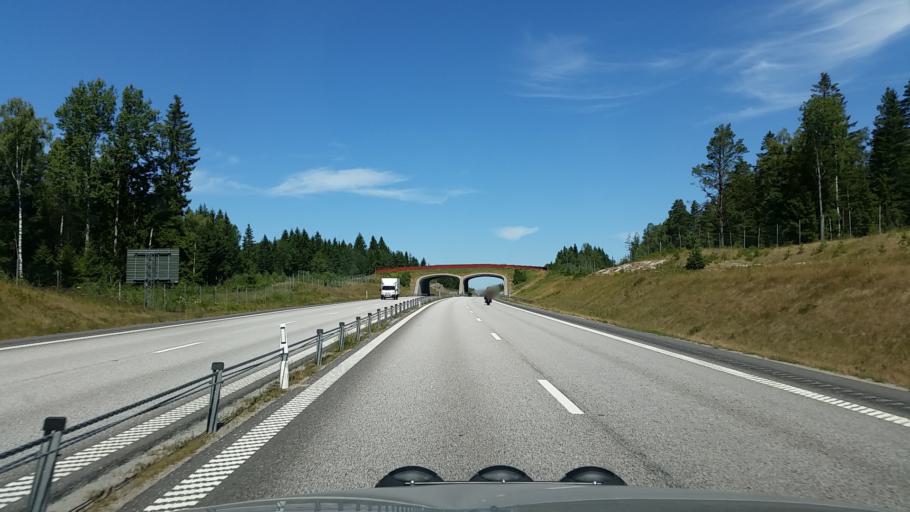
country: SE
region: Vaestra Goetaland
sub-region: Lilla Edets Kommun
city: Lodose
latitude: 58.0513
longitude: 12.1693
